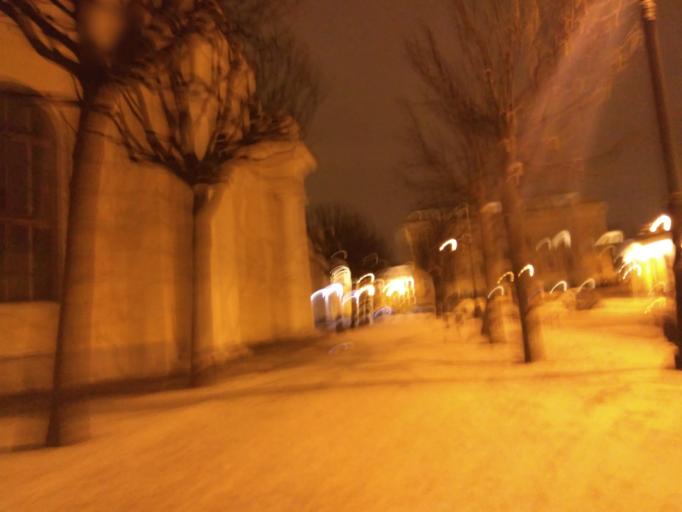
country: RU
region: St.-Petersburg
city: Centralniy
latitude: 59.9372
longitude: 30.3400
